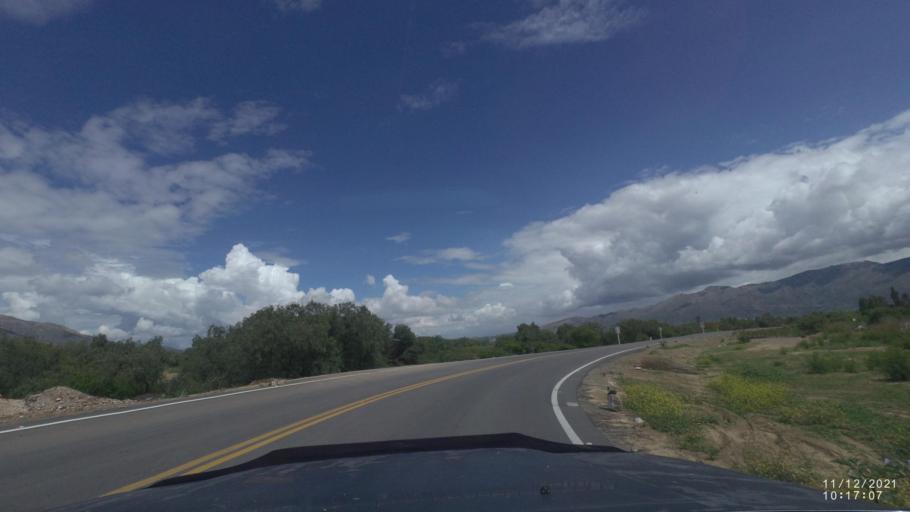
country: BO
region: Cochabamba
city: Tarata
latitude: -17.5895
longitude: -66.0201
